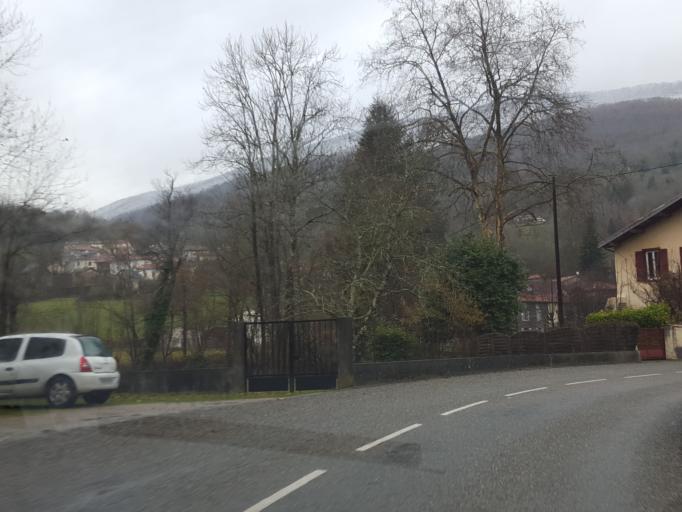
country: FR
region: Midi-Pyrenees
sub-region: Departement de l'Ariege
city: Saint-Girons
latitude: 42.9075
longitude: 1.2493
